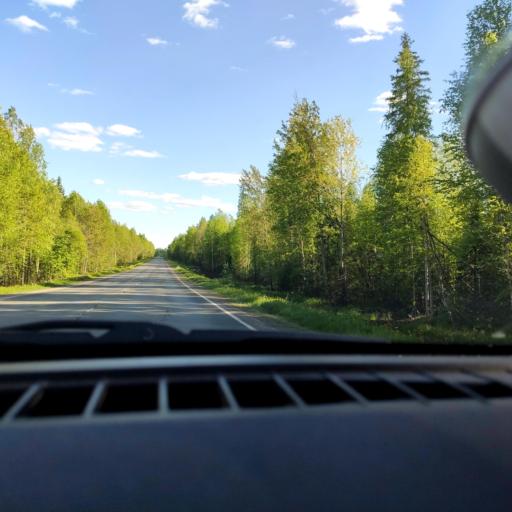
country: RU
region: Perm
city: Polazna
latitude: 58.2779
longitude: 56.1656
